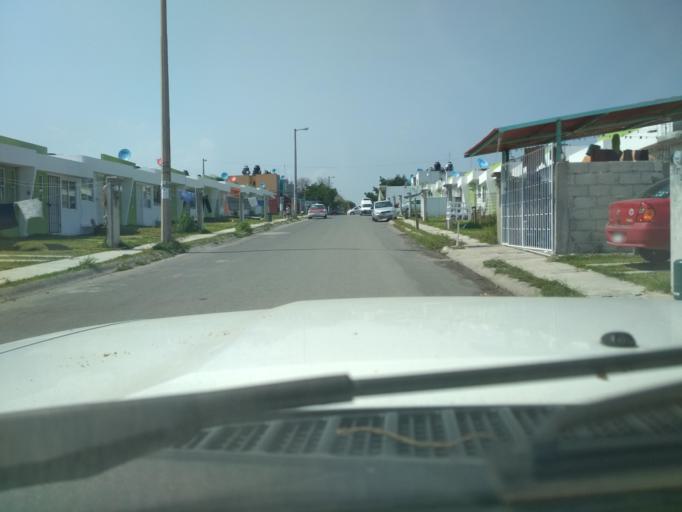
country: MX
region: Veracruz
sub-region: Veracruz
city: Lomas de Rio Medio Cuatro
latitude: 19.1942
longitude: -96.2084
